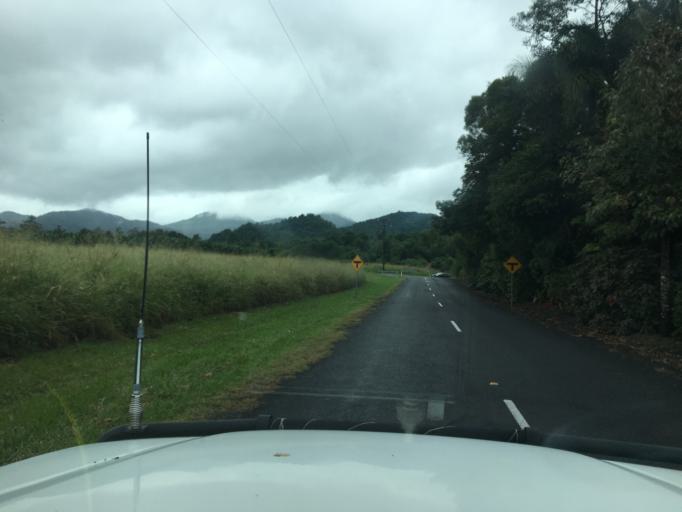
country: AU
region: Queensland
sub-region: Cassowary Coast
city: Innisfail
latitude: -17.4421
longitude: 145.8609
